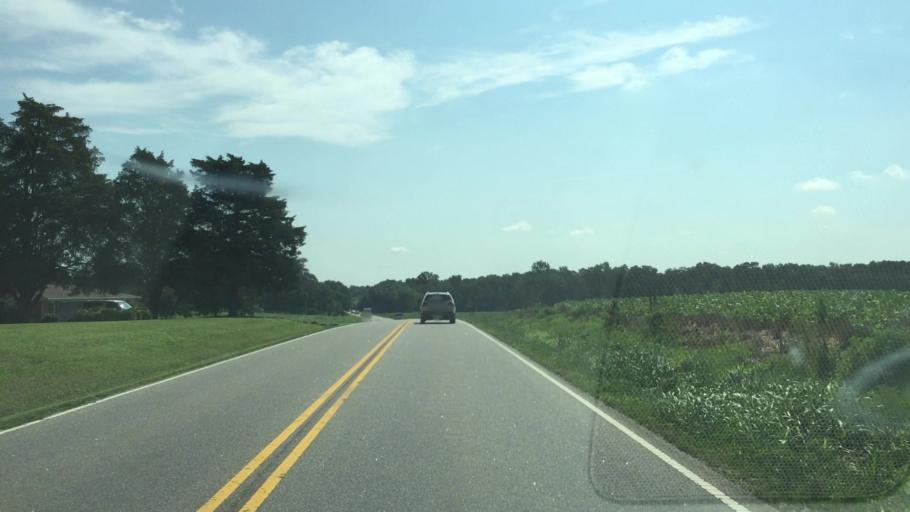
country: US
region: North Carolina
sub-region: Stanly County
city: Stanfield
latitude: 35.1294
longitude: -80.3979
